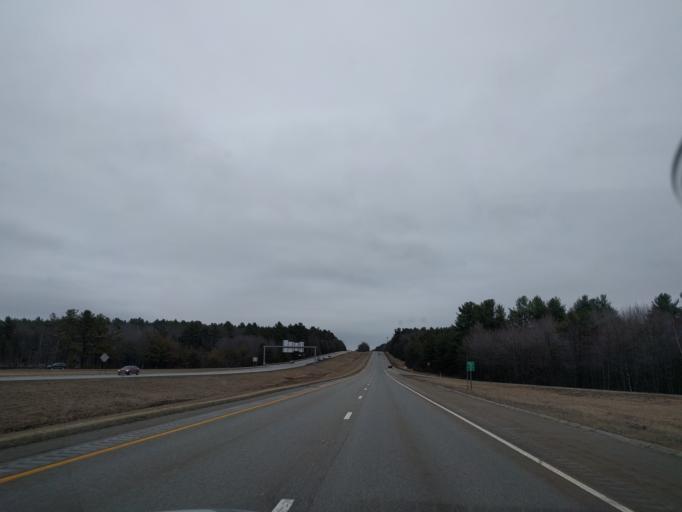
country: US
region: Massachusetts
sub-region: Worcester County
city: Phillipston
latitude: 42.5707
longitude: -72.1265
